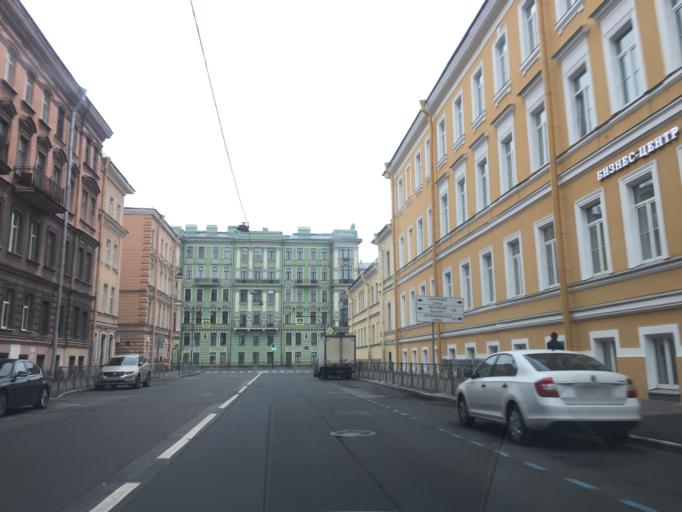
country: RU
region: St.-Petersburg
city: Centralniy
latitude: 59.9431
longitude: 30.3638
